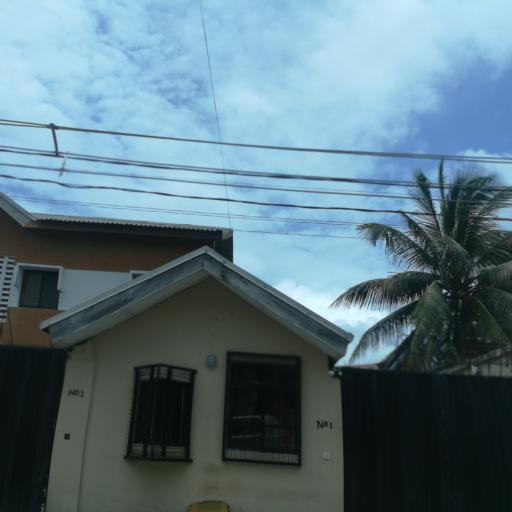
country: NG
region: Lagos
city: Ikoyi
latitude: 6.4386
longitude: 3.4650
